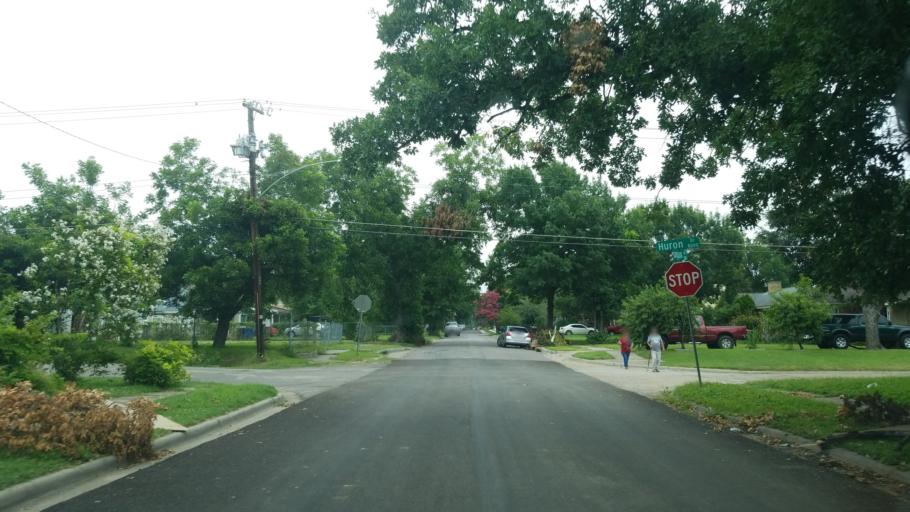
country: US
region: Texas
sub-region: Dallas County
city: University Park
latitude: 32.8358
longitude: -96.8605
